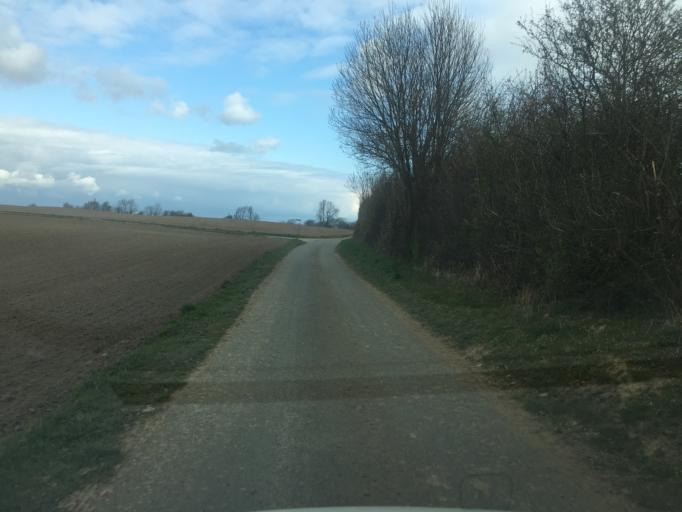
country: DK
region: South Denmark
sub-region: Sonderborg Kommune
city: Grasten
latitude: 54.9995
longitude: 9.5303
